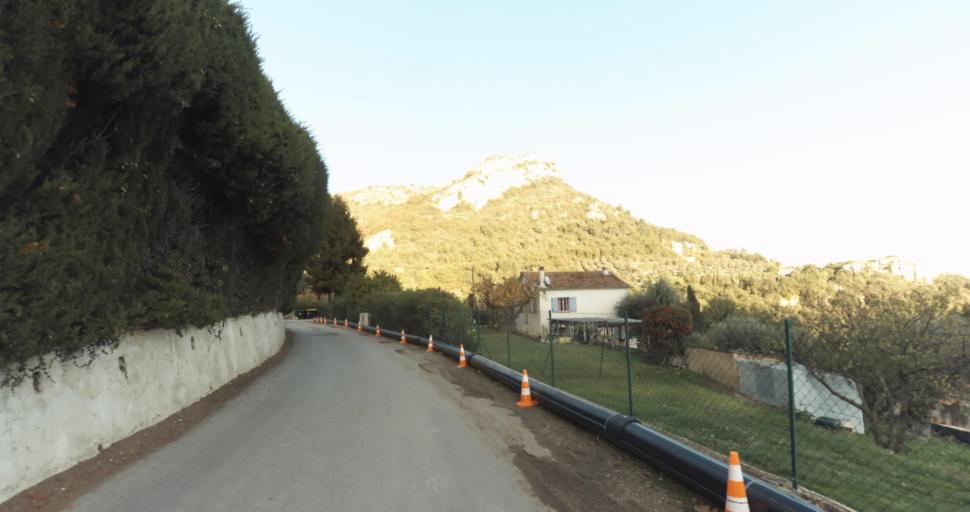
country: FR
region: Provence-Alpes-Cote d'Azur
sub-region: Departement des Alpes-Maritimes
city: Vence
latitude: 43.7325
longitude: 7.1006
